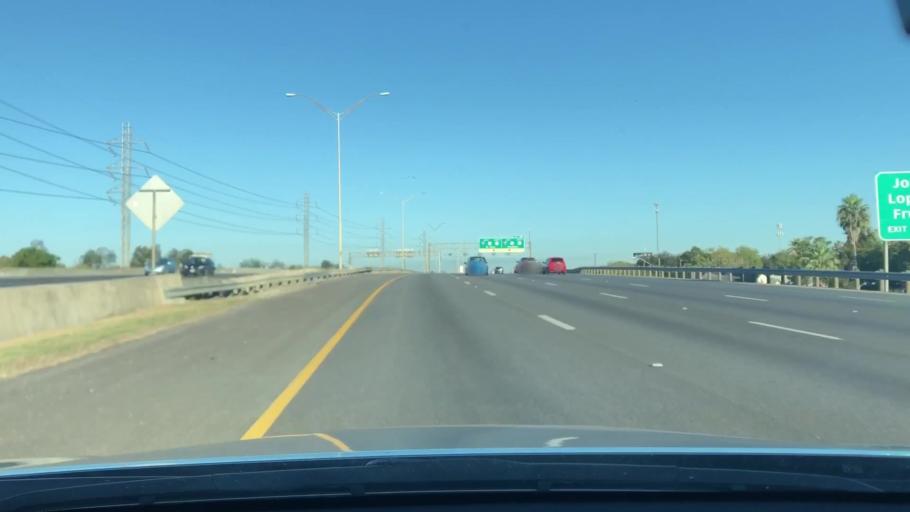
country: US
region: Texas
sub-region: Bexar County
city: San Antonio
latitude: 29.3869
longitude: -98.4724
